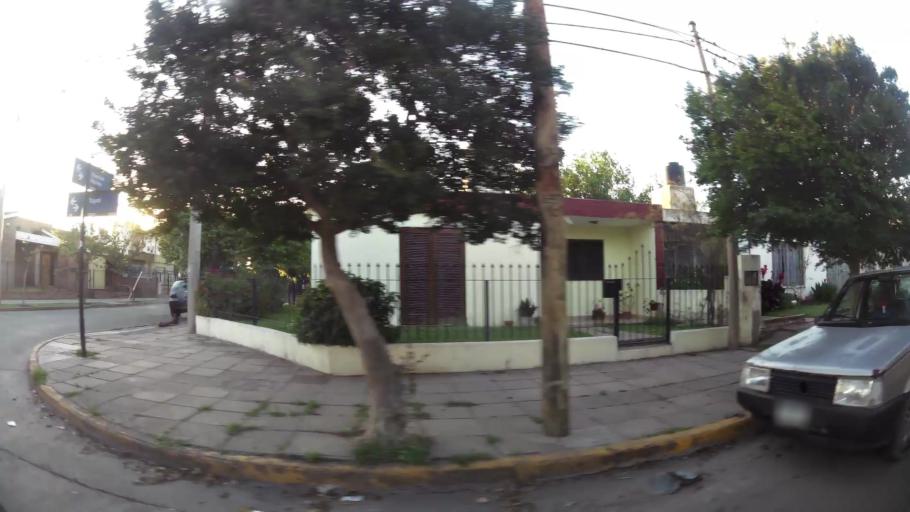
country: AR
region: Cordoba
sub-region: Departamento de Capital
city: Cordoba
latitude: -31.3770
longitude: -64.2125
